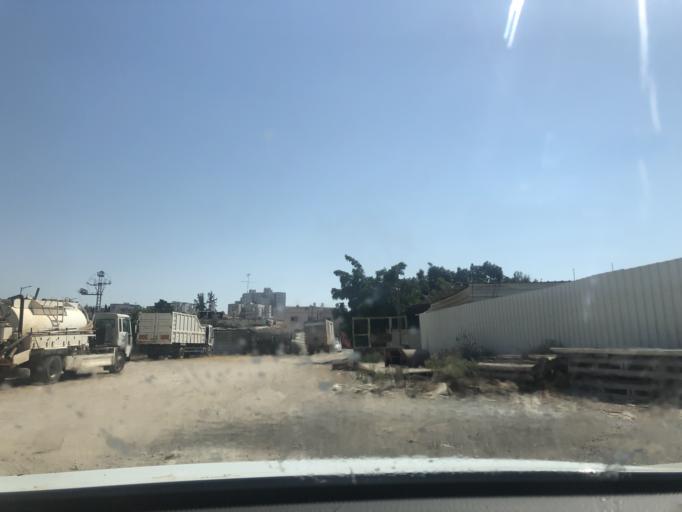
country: IL
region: Central District
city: Lod
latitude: 31.9593
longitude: 34.8968
